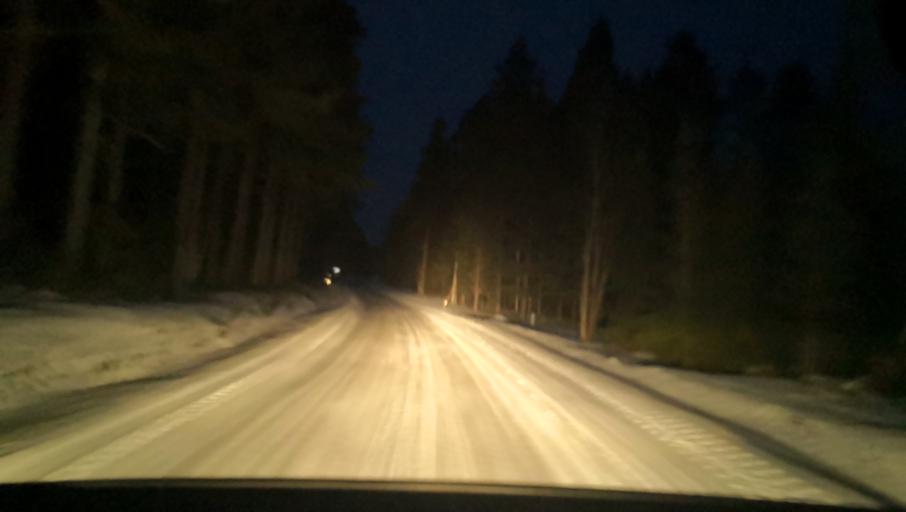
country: SE
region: Uppsala
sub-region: Heby Kommun
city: Tarnsjo
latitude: 60.2801
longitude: 16.8035
